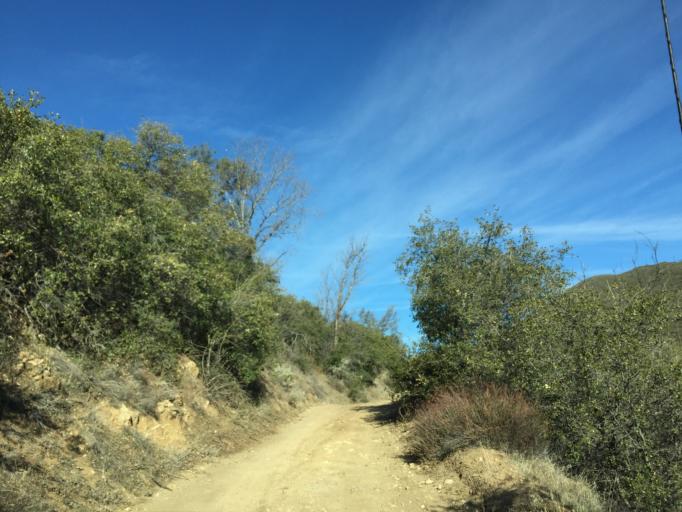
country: US
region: California
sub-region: Riverside County
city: Anza
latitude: 33.5949
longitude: -116.7775
